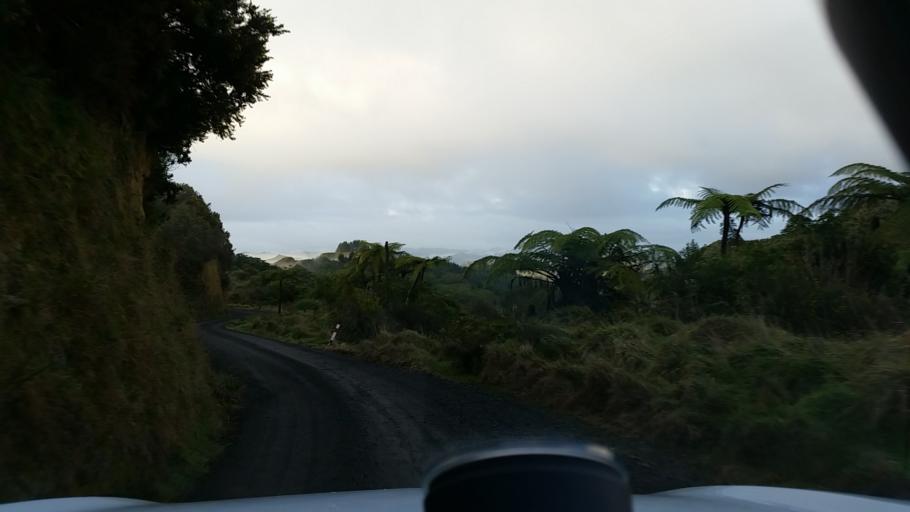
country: NZ
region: Taranaki
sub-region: South Taranaki District
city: Eltham
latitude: -39.4471
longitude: 174.4541
